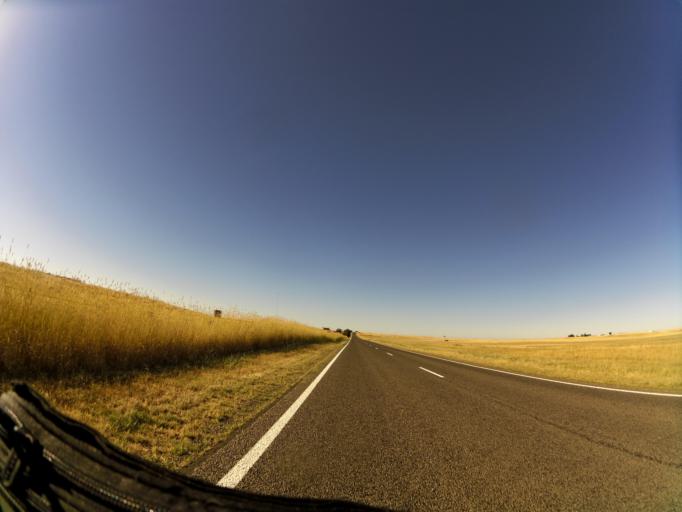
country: AU
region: Victoria
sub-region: Ballarat North
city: Delacombe
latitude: -37.5904
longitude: 143.3533
